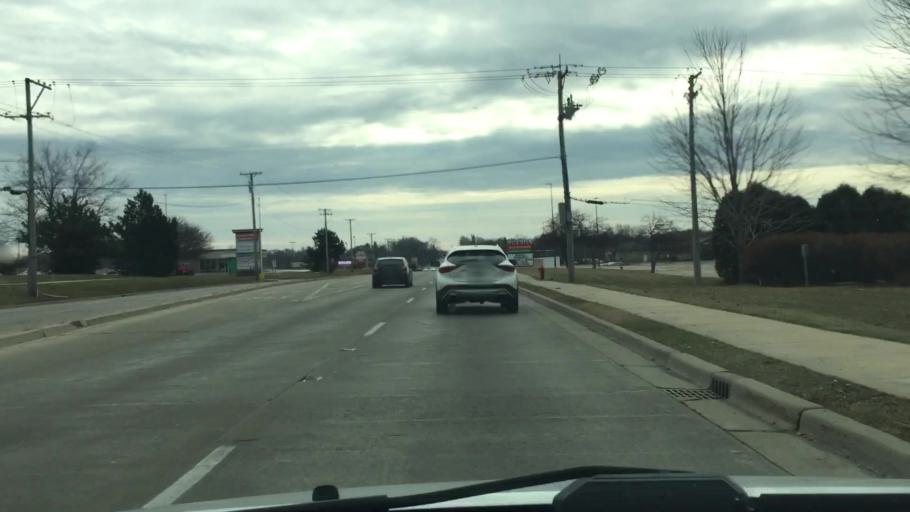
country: US
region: Illinois
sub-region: McHenry County
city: McHenry
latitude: 42.3577
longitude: -88.2673
